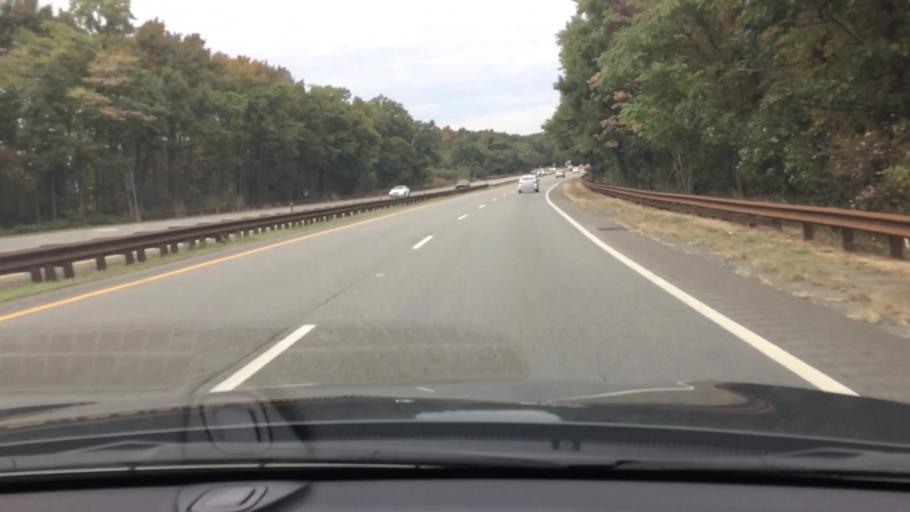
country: US
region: New Jersey
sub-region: Bergen County
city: Englewood Cliffs
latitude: 40.8769
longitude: -73.9500
